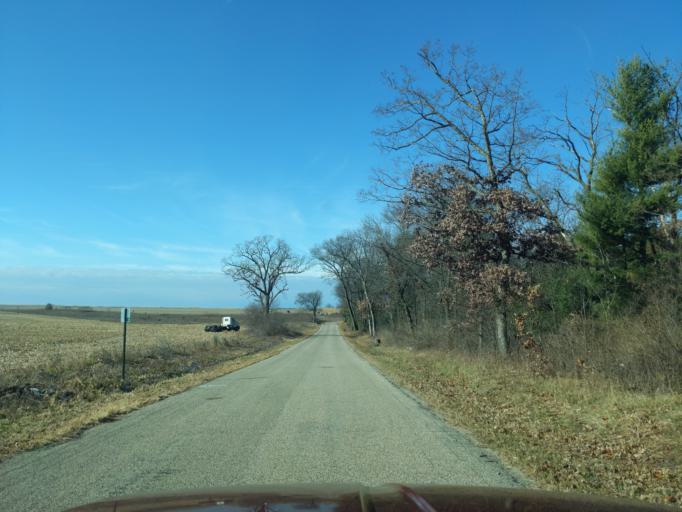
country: US
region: Wisconsin
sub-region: Waushara County
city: Silver Lake
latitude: 44.0979
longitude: -89.1745
